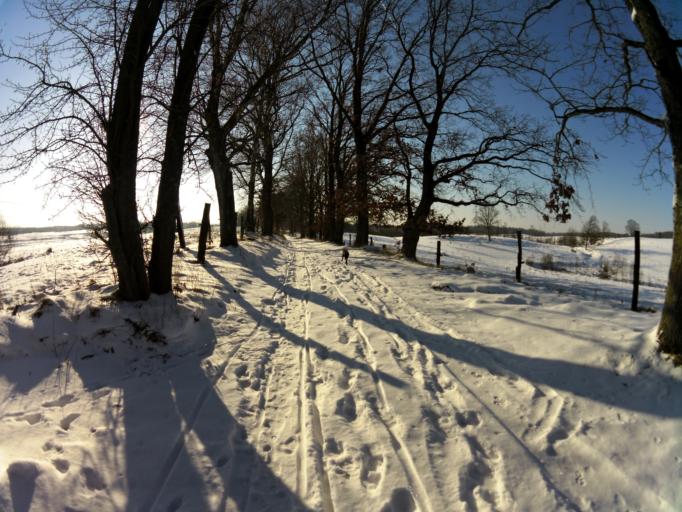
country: PL
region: West Pomeranian Voivodeship
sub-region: Powiat stargardzki
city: Dobrzany
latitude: 53.3829
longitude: 15.4845
